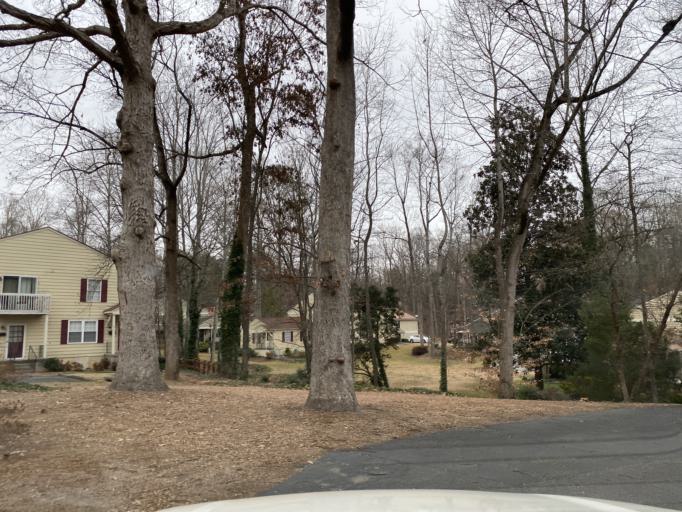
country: US
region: Georgia
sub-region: Cobb County
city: Fair Oaks
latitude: 33.9185
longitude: -84.5730
